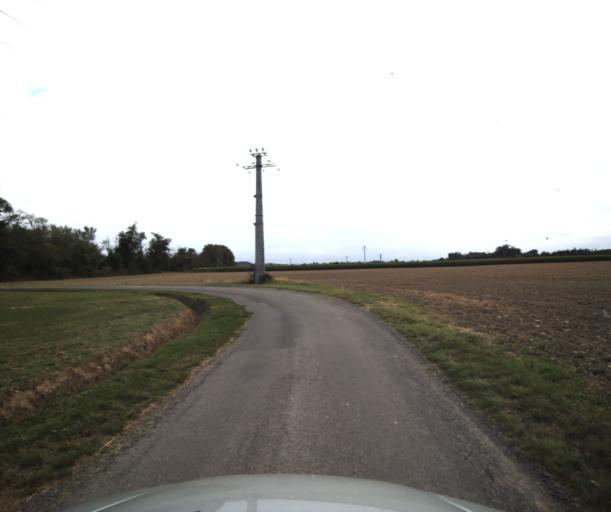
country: FR
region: Midi-Pyrenees
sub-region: Departement de la Haute-Garonne
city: Le Fauga
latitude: 43.4182
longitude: 1.3055
